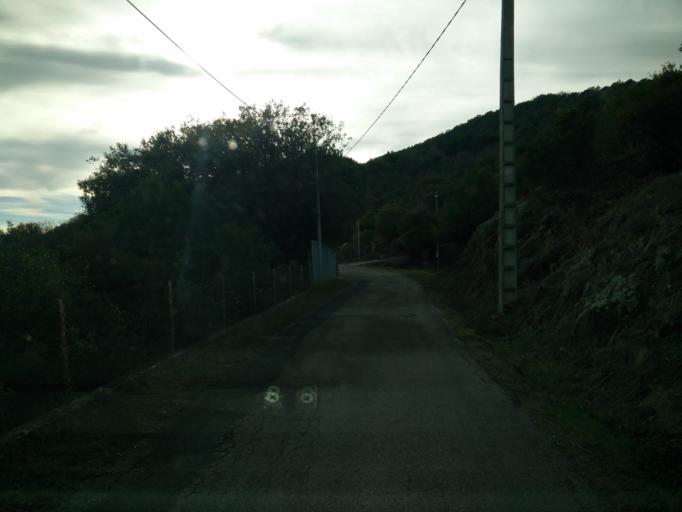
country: FR
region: Provence-Alpes-Cote d'Azur
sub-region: Departement du Var
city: Roquebrune-sur-Argens
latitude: 43.4308
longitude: 6.6392
